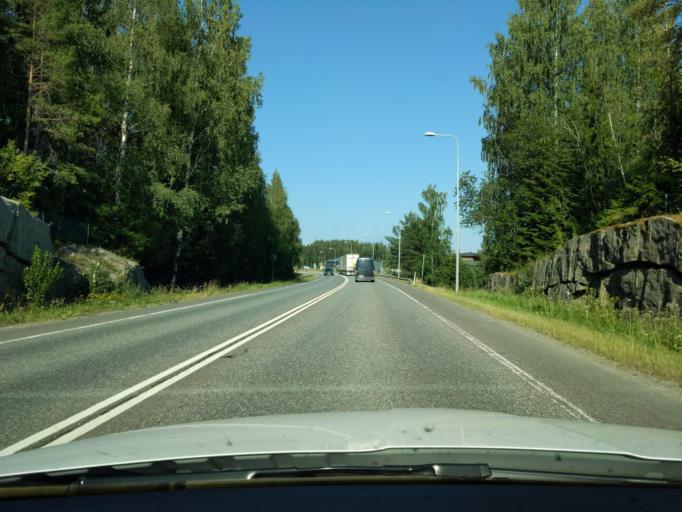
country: FI
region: Paijanne Tavastia
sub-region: Lahti
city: Hollola
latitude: 60.9733
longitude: 25.4763
